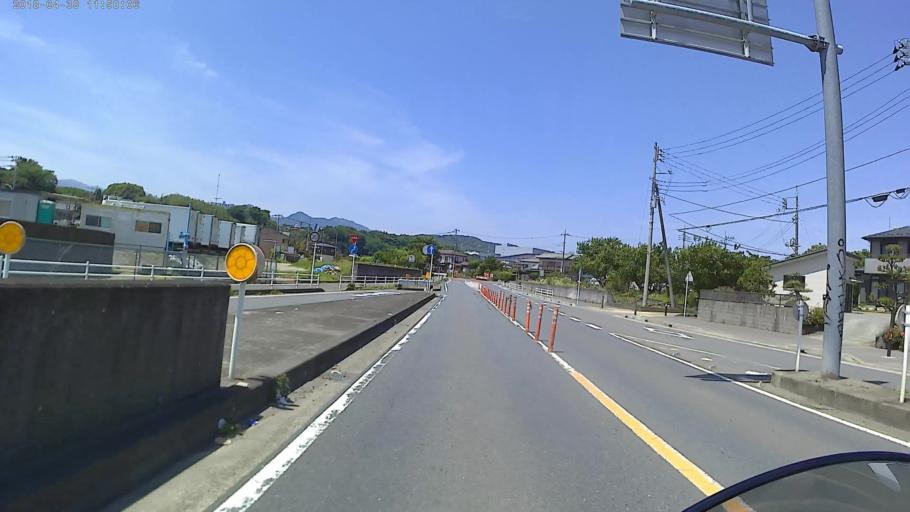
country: JP
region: Kanagawa
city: Zama
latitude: 35.4840
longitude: 139.3525
